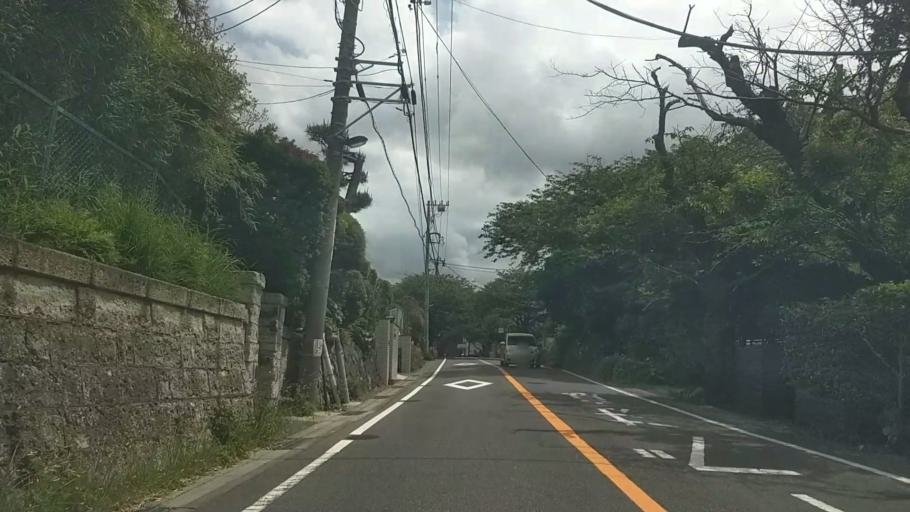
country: JP
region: Kanagawa
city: Kamakura
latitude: 35.3167
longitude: 139.5177
